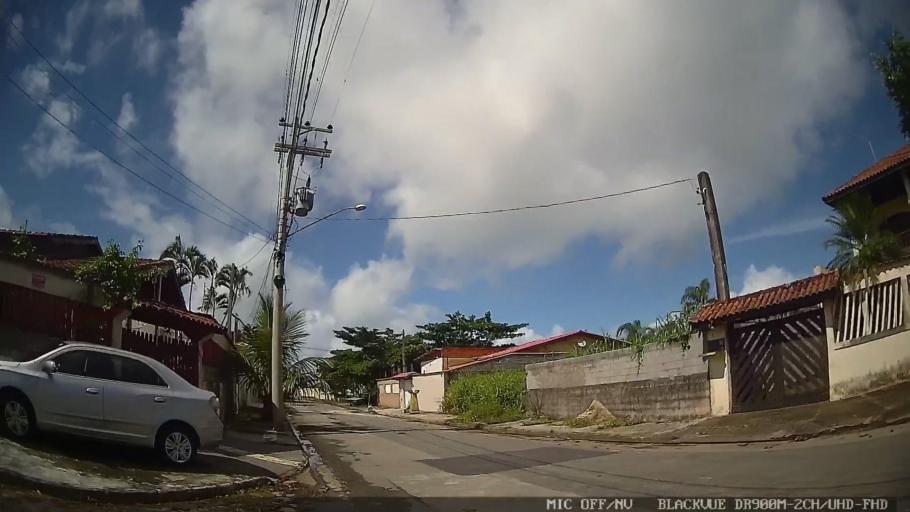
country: BR
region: Sao Paulo
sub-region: Itanhaem
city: Itanhaem
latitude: -24.2228
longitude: -46.8589
